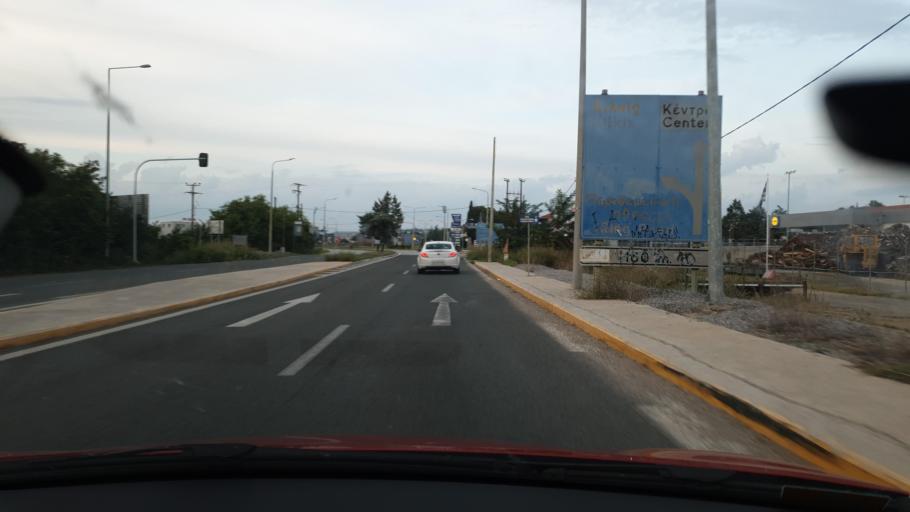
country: GR
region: Central Macedonia
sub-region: Nomos Kilkis
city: Kilkis
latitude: 40.9810
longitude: 22.8628
